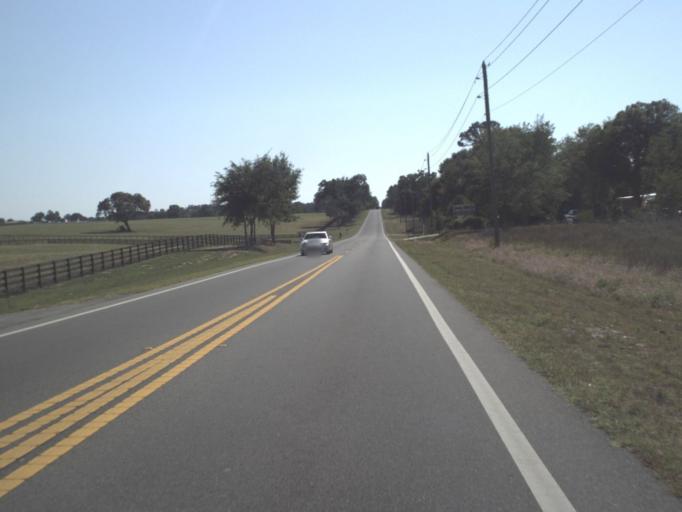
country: US
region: Florida
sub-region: Marion County
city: Dunnellon
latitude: 29.1561
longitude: -82.3557
